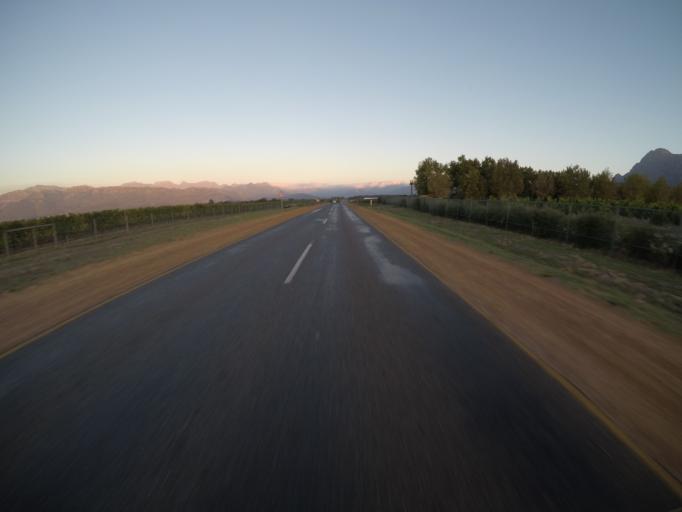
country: ZA
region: Western Cape
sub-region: Cape Winelands District Municipality
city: Paarl
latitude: -33.8206
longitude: 18.9266
